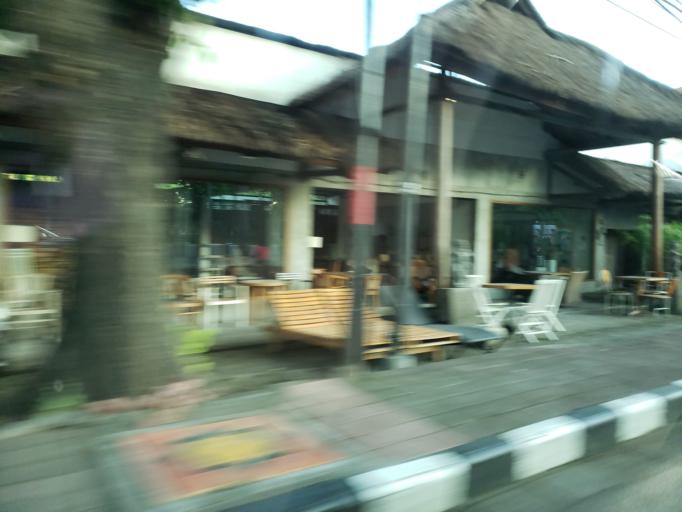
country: ID
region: Bali
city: Kelanabian
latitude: -8.7561
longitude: 115.1798
